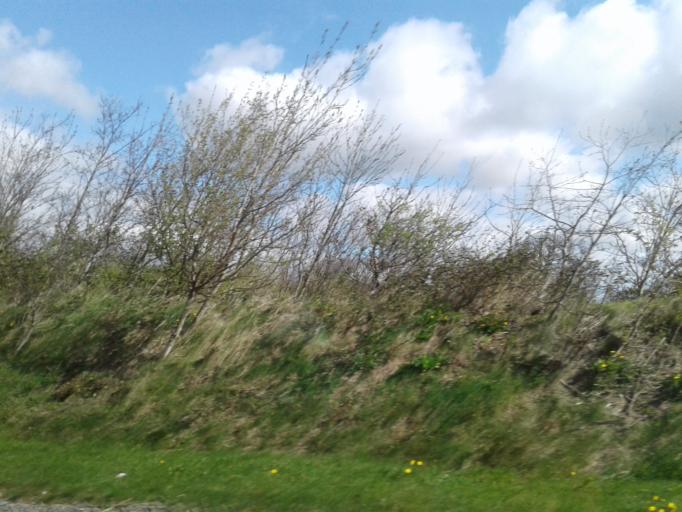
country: IE
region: Leinster
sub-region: An Mhi
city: Ashbourne
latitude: 53.4671
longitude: -6.3612
